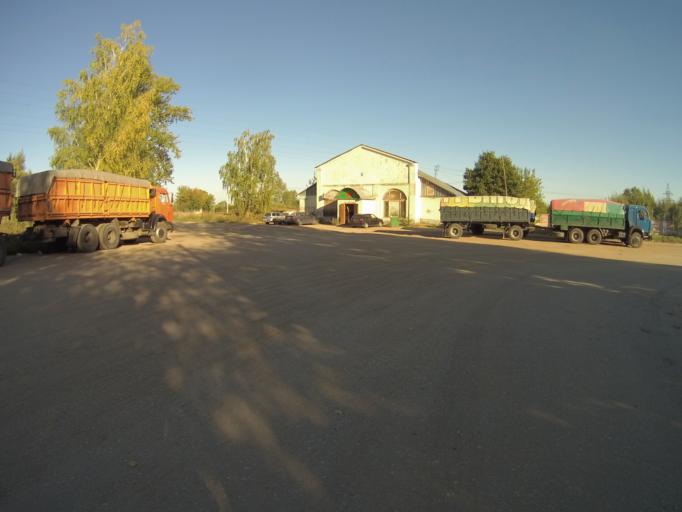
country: RU
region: Vladimir
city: Vladimir
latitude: 56.1033
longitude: 40.3721
